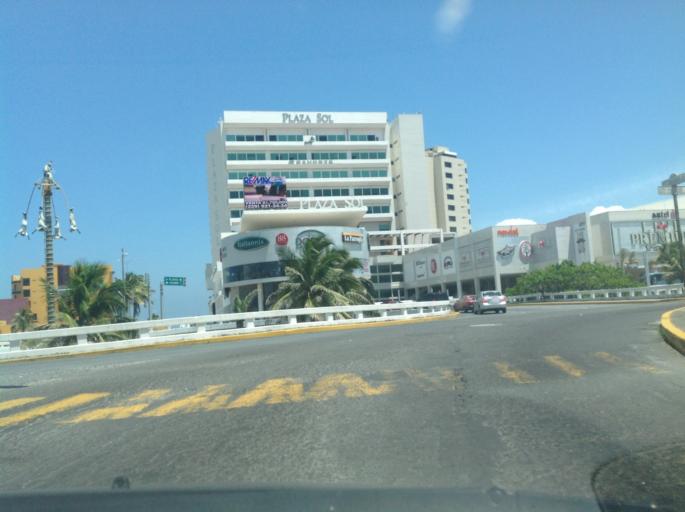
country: MX
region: Veracruz
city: Boca del Rio
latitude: 19.1410
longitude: -96.1042
